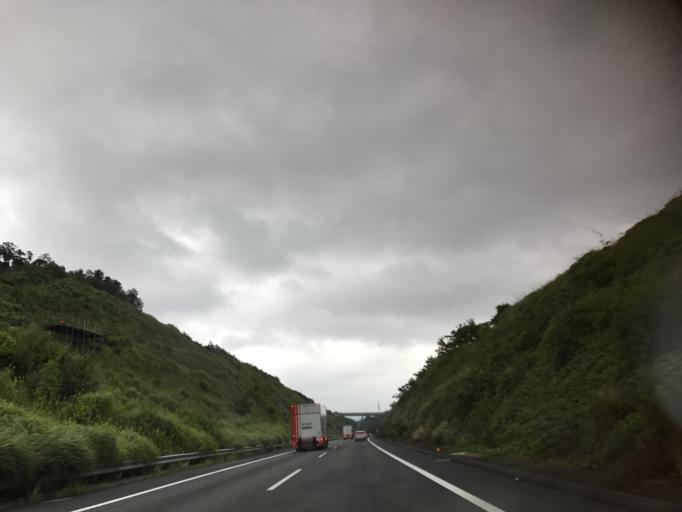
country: JP
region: Shizuoka
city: Fujinomiya
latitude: 35.1882
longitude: 138.6204
